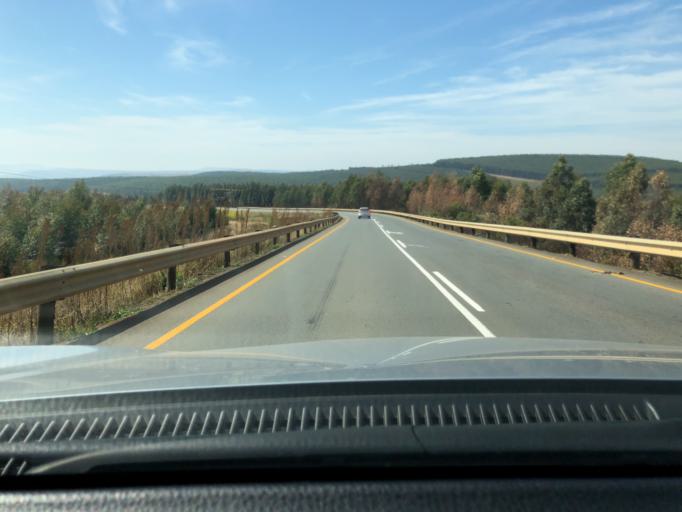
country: ZA
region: KwaZulu-Natal
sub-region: Sisonke District Municipality
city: Ixopo
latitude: -30.1026
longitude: 30.1290
